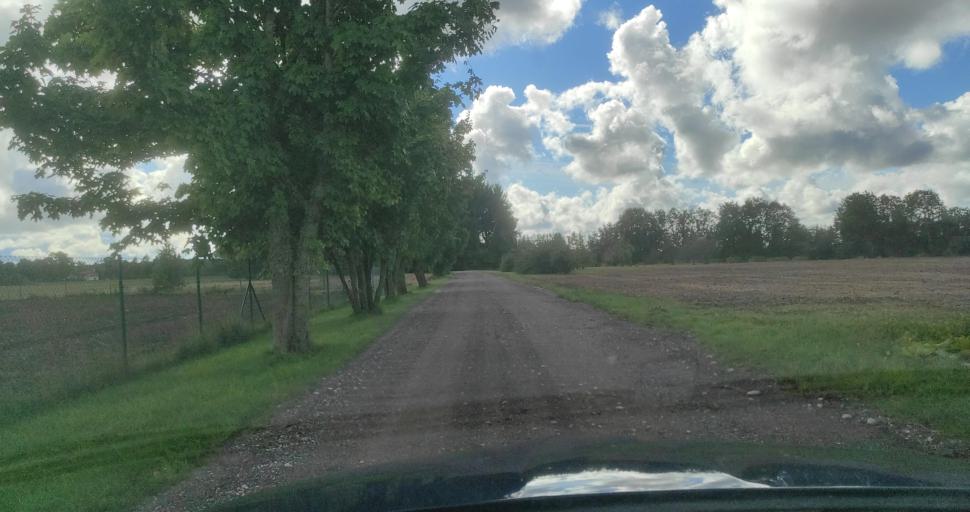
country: LV
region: Ventspils Rajons
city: Piltene
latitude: 57.2656
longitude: 21.6035
